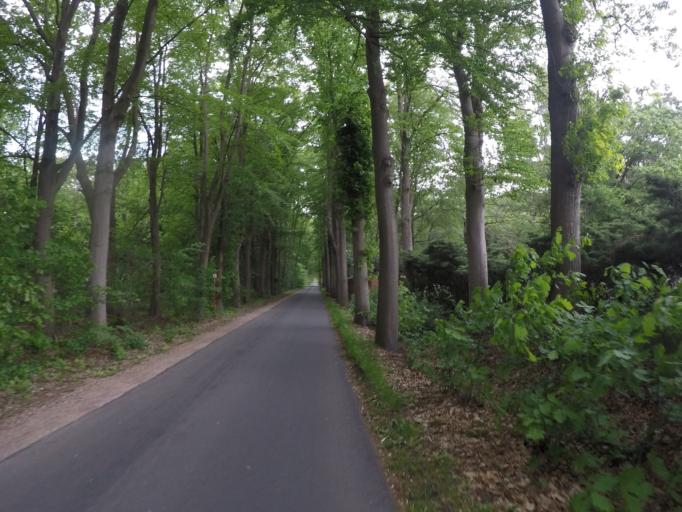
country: BE
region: Flanders
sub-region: Provincie Antwerpen
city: Zoersel
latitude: 51.2793
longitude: 4.6551
